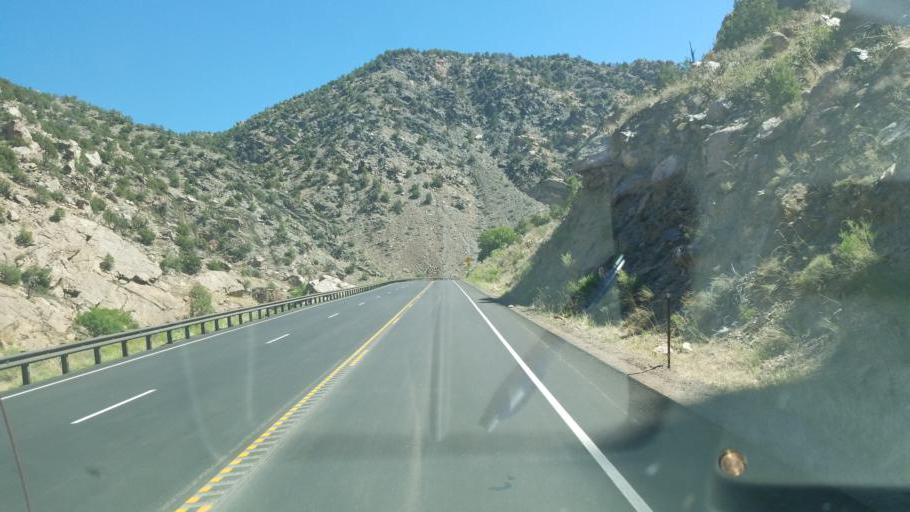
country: US
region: Colorado
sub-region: Custer County
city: Westcliffe
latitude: 38.4272
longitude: -105.5537
